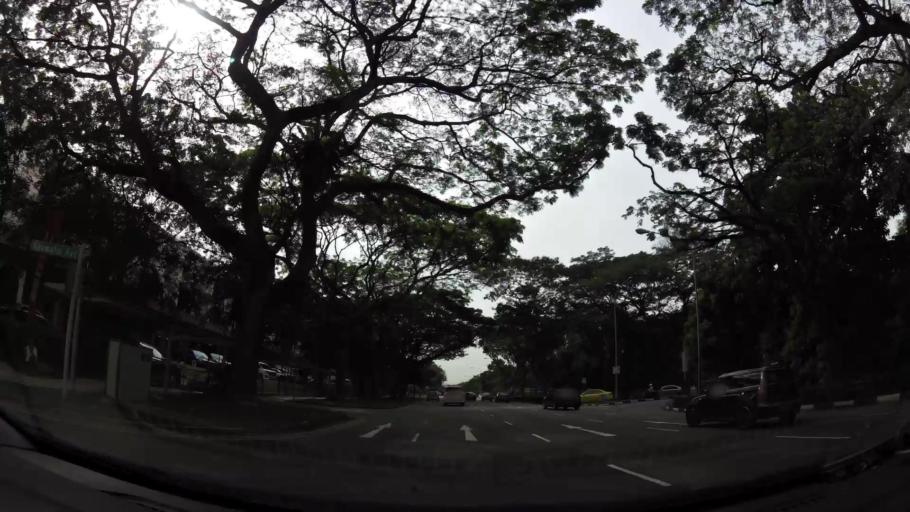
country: SG
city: Singapore
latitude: 1.3318
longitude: 103.7944
